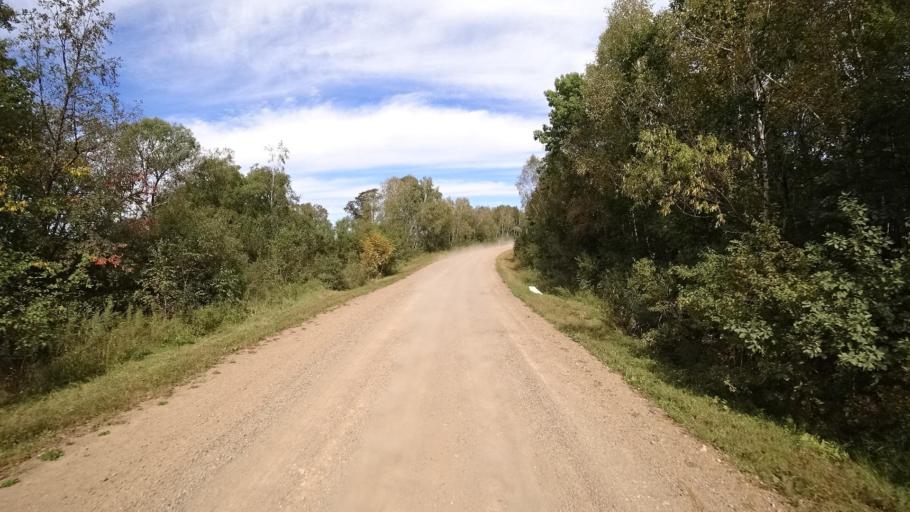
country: RU
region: Primorskiy
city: Yakovlevka
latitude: 44.6943
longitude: 133.6193
